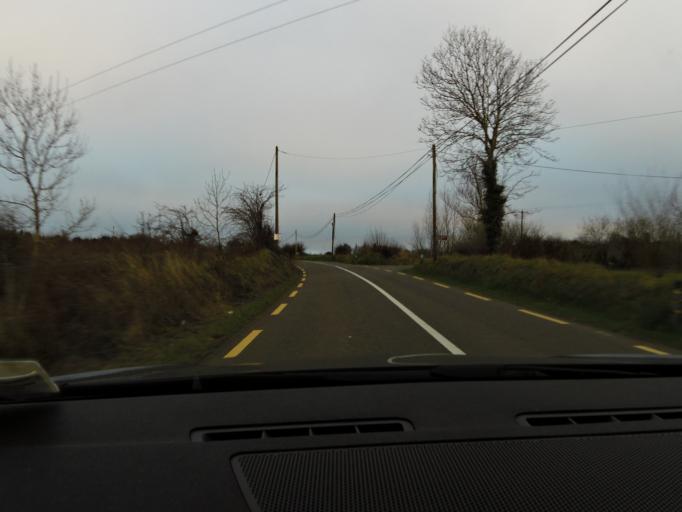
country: IE
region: Connaught
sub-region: Sligo
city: Ballymote
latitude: 54.0070
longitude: -8.5458
